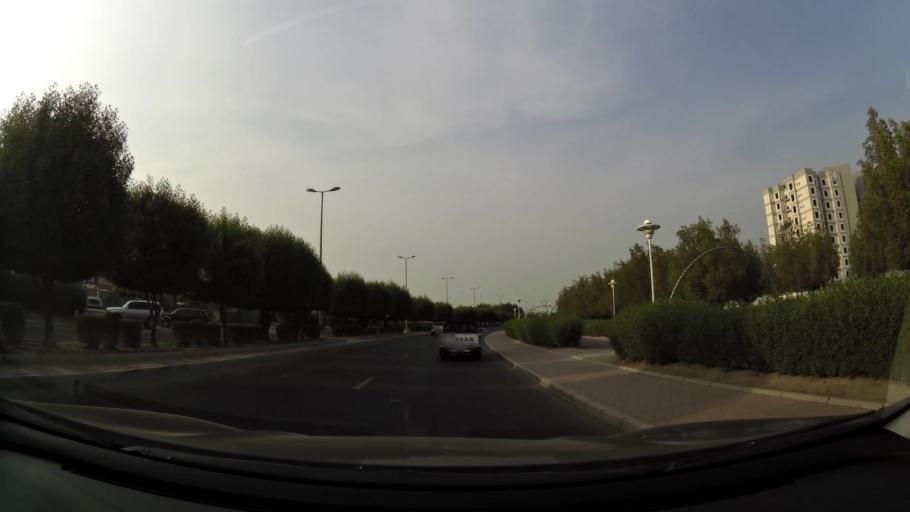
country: KW
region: Mubarak al Kabir
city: Sabah as Salim
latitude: 29.2545
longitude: 48.0785
